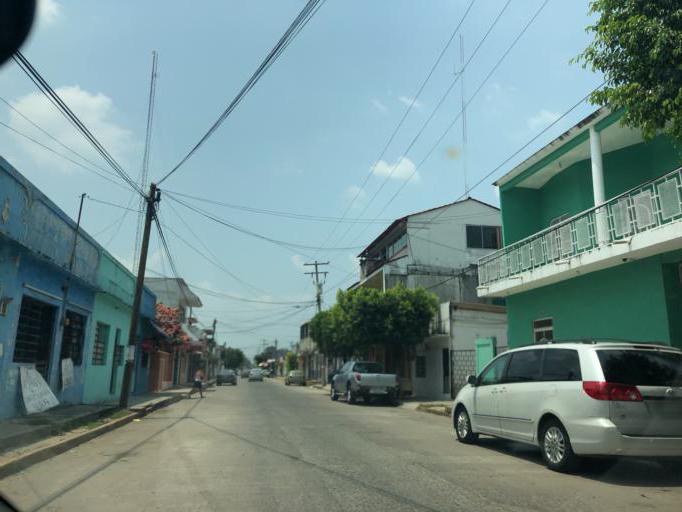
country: MX
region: Tabasco
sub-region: Cardenas
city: Cardenas
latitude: 17.9884
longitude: -93.3818
